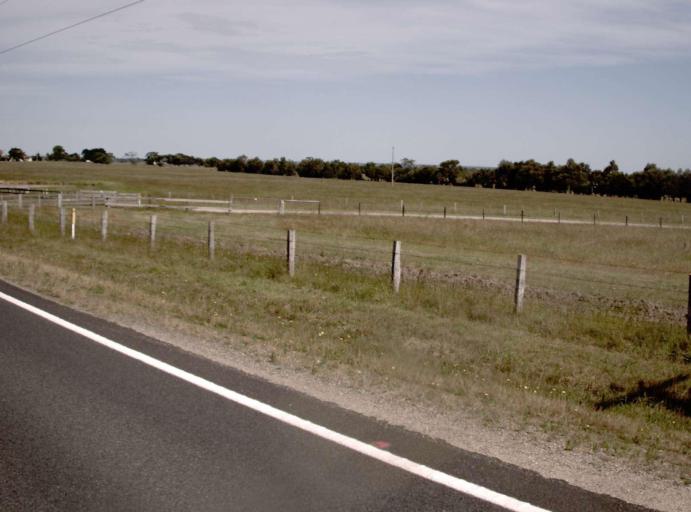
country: AU
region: Victoria
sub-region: East Gippsland
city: Bairnsdale
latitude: -37.8251
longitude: 147.7010
